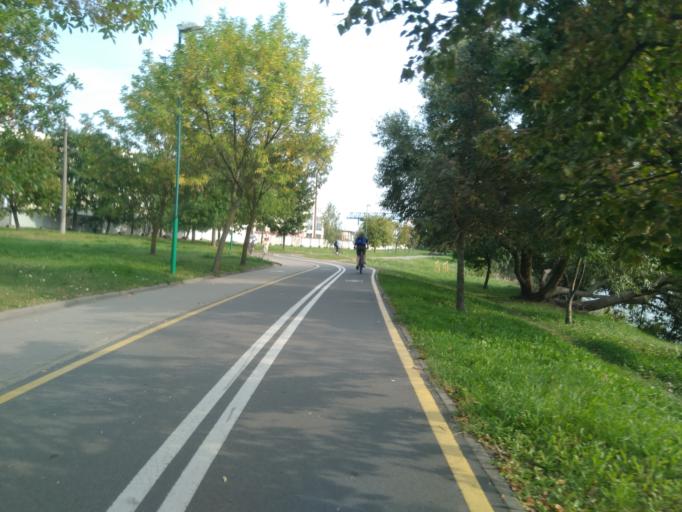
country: BY
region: Minsk
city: Minsk
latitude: 53.8824
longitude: 27.5742
